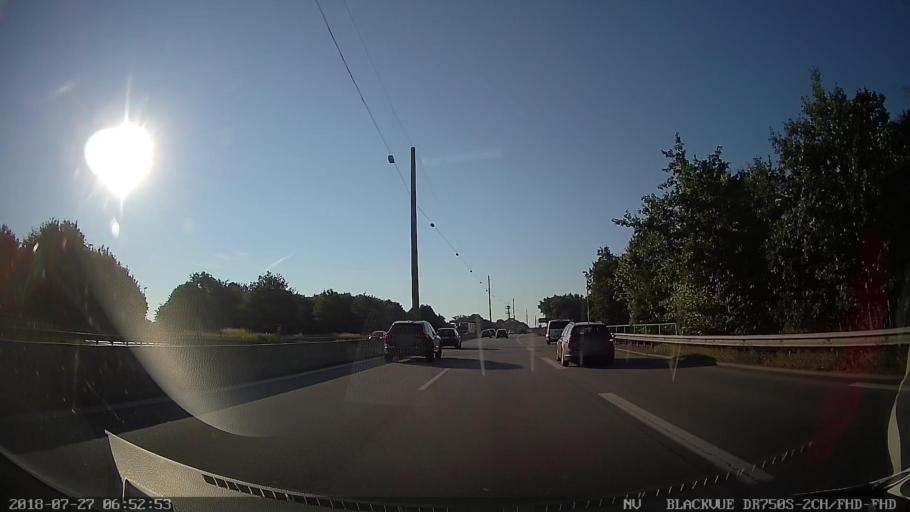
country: DE
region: Hamburg
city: Eidelstedt
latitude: 53.6212
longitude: 9.9043
